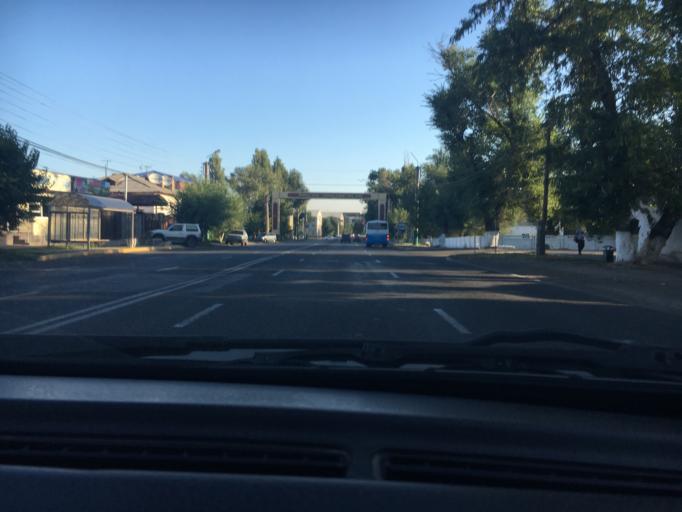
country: KZ
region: Zhambyl
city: Taraz
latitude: 42.8985
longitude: 71.3602
